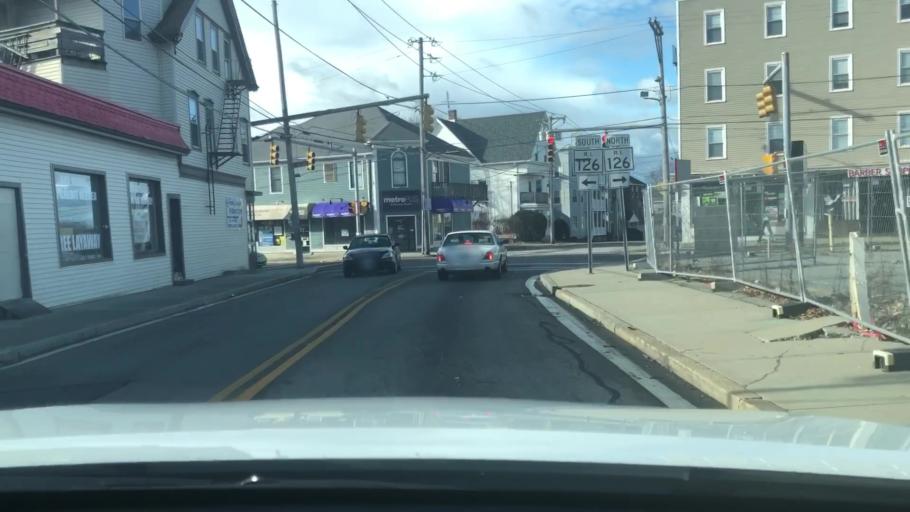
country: US
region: Rhode Island
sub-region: Providence County
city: Woonsocket
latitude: 42.0157
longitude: -71.4998
